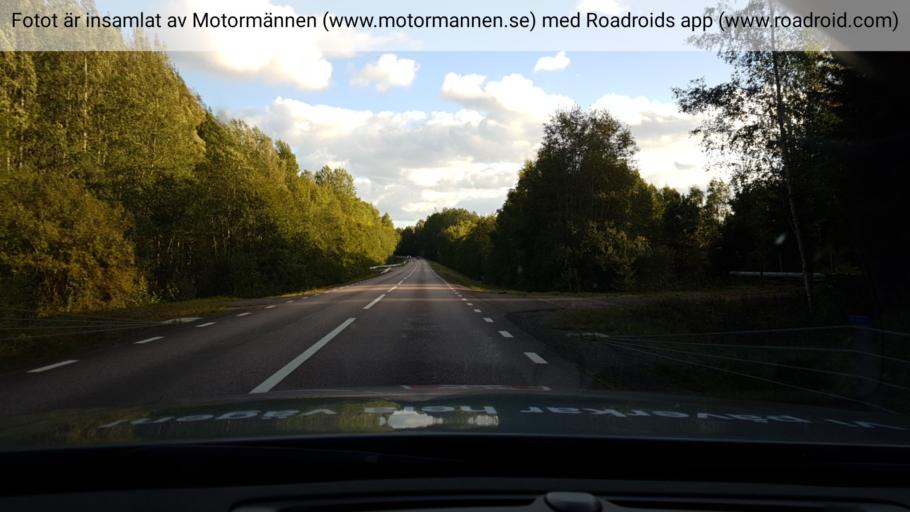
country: SE
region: Vaermland
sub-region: Karlstads Kommun
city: Molkom
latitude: 59.6536
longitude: 13.7109
